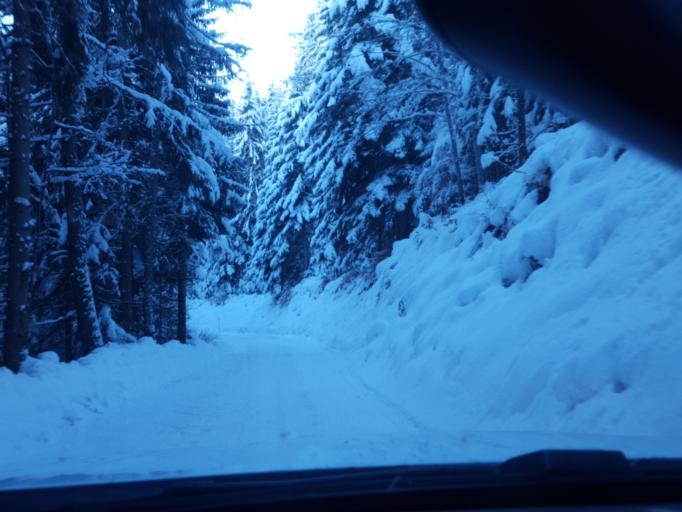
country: FR
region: Rhone-Alpes
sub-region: Departement de la Savoie
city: Salins-les-Thermes
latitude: 45.4744
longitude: 6.5137
